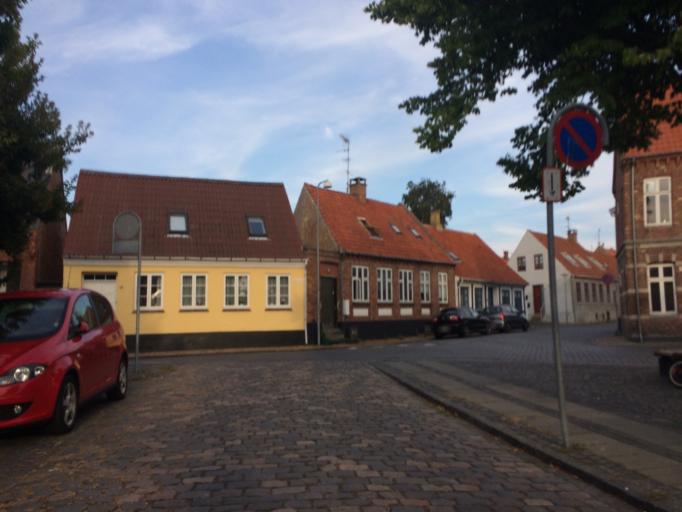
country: DK
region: Capital Region
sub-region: Bornholm Kommune
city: Ronne
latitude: 55.1017
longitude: 14.7022
